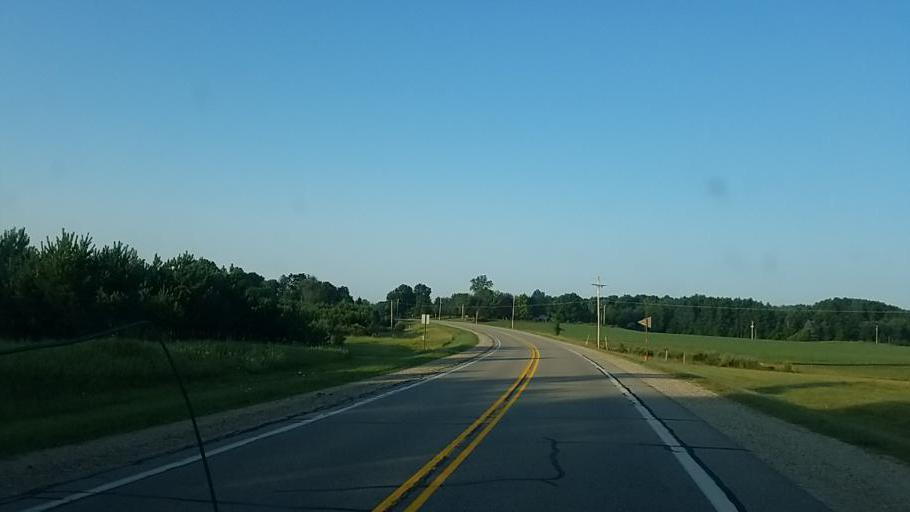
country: US
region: Michigan
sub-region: Montcalm County
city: Edmore
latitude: 43.4474
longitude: -85.1478
